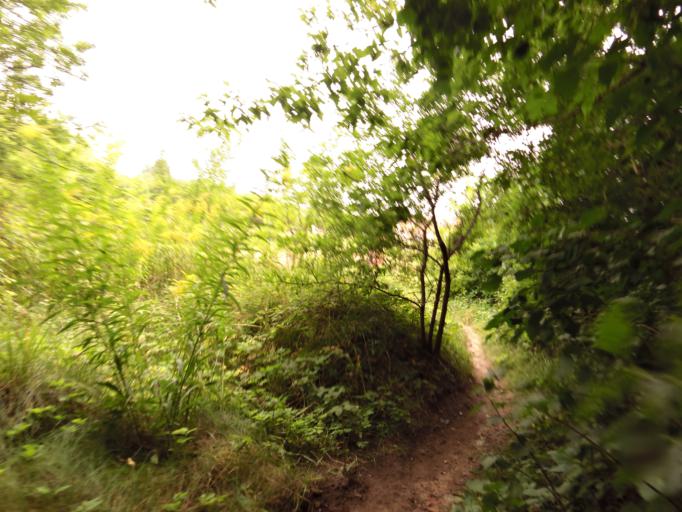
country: LT
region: Vilnius County
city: Naujamiestis
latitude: 54.6607
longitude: 25.2882
